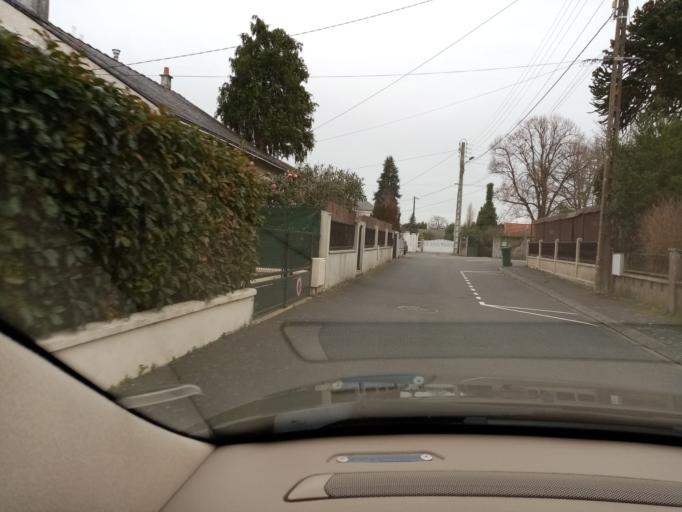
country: FR
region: Pays de la Loire
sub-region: Departement de la Loire-Atlantique
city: Saint-Sebastien-sur-Loire
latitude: 47.2043
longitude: -1.5097
